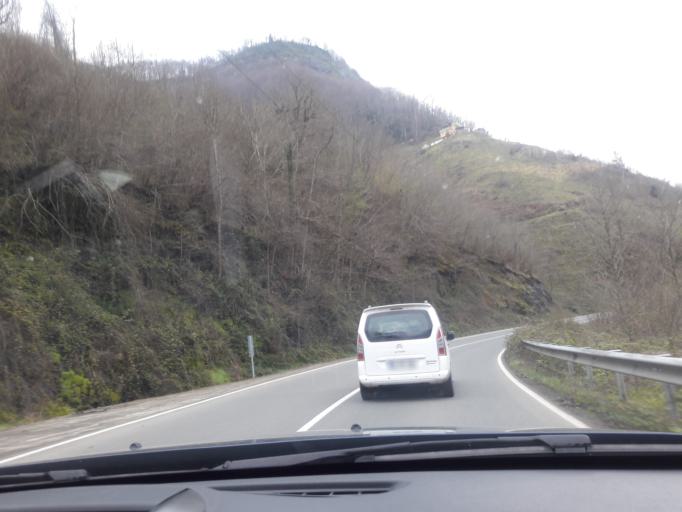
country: TR
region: Trabzon
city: Salpazari
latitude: 40.9778
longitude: 39.1980
